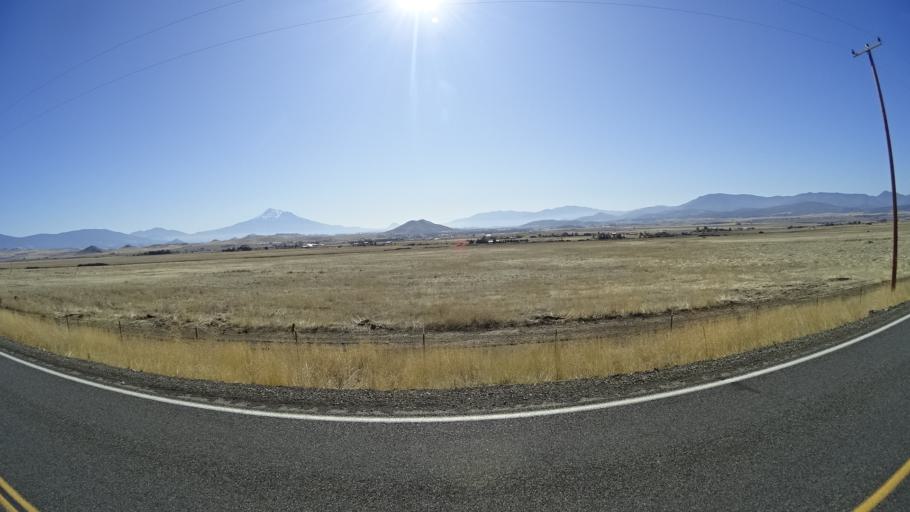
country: US
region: California
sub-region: Siskiyou County
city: Montague
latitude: 41.7714
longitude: -122.5363
